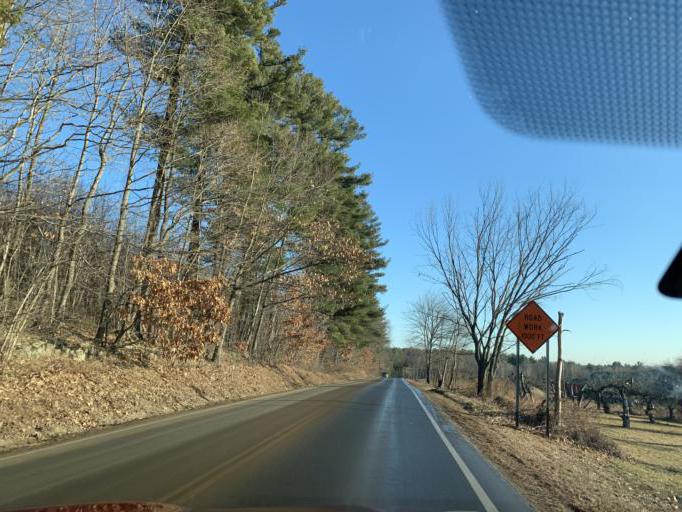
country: US
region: New Hampshire
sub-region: Rockingham County
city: Derry
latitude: 42.8778
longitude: -71.3501
